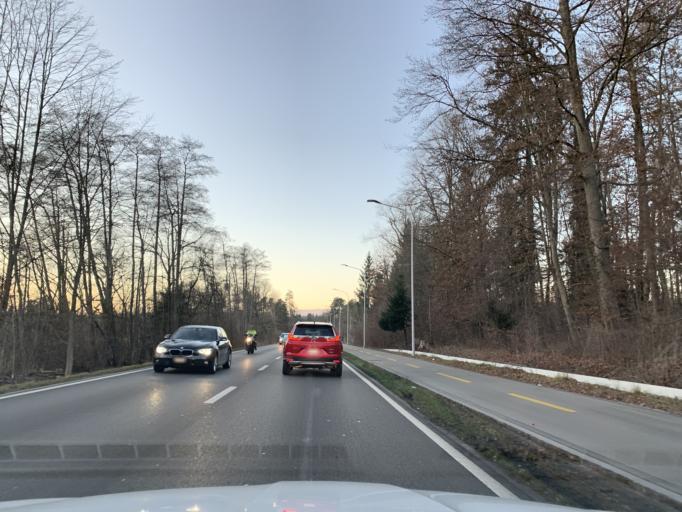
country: CH
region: Zurich
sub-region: Bezirk Zuerich
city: Zuerich (Kreis 10) / Ruetihof
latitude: 47.4294
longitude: 8.4879
